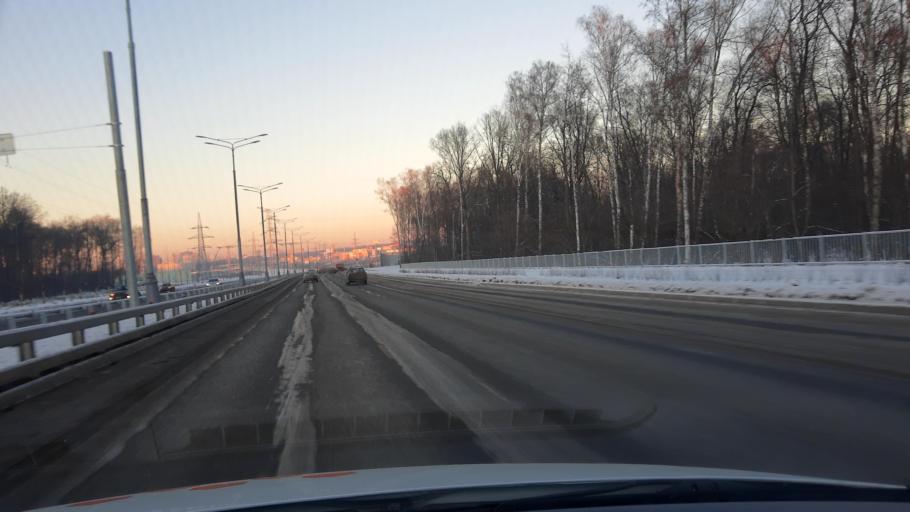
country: RU
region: Moskovskaya
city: Kommunarka
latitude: 55.5889
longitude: 37.4816
